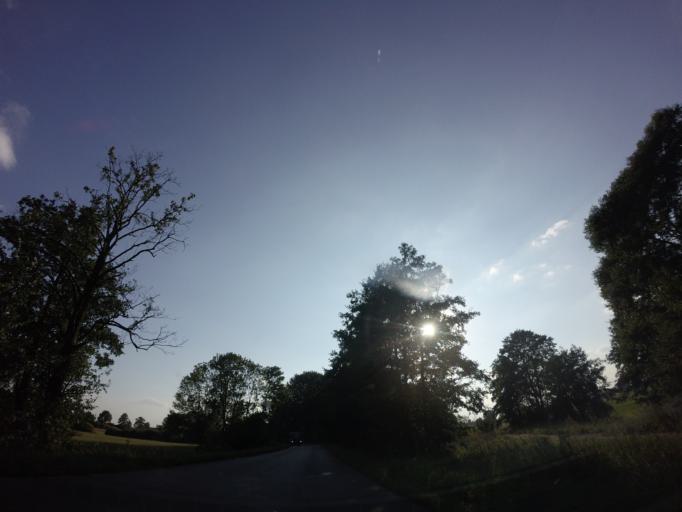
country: PL
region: Lublin Voivodeship
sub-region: Powiat lubartowski
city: Abramow
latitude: 51.4677
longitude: 22.2832
